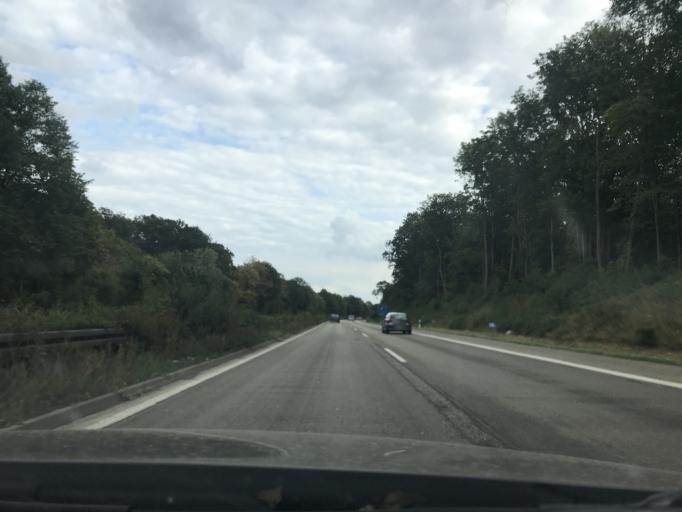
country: DE
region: North Rhine-Westphalia
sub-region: Regierungsbezirk Dusseldorf
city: Hilden
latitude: 51.1669
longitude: 6.8871
